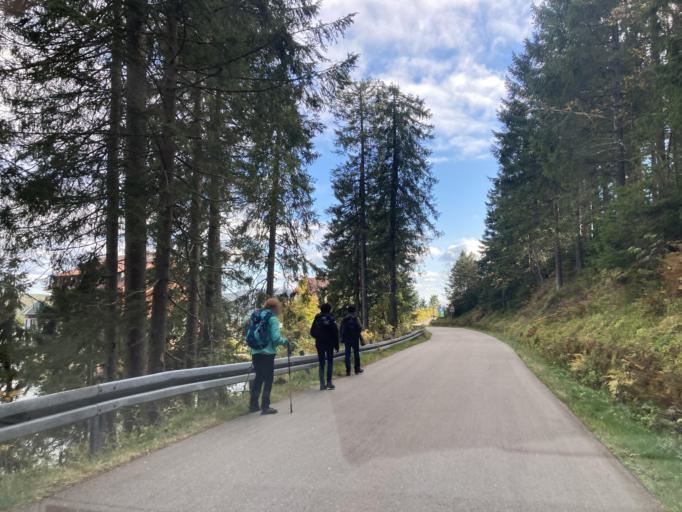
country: DE
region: Baden-Wuerttemberg
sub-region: Freiburg Region
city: Seebach
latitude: 48.5973
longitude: 8.1996
